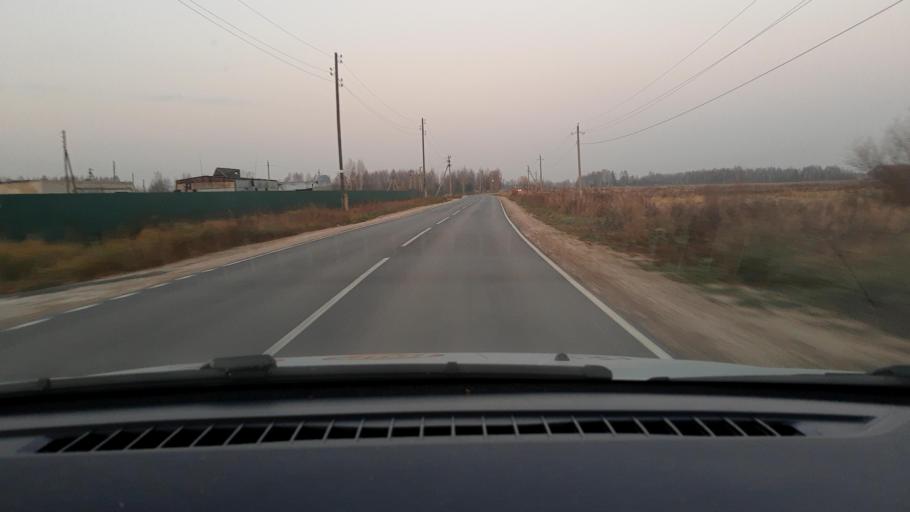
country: RU
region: Nizjnij Novgorod
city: Neklyudovo
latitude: 56.4505
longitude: 43.9009
